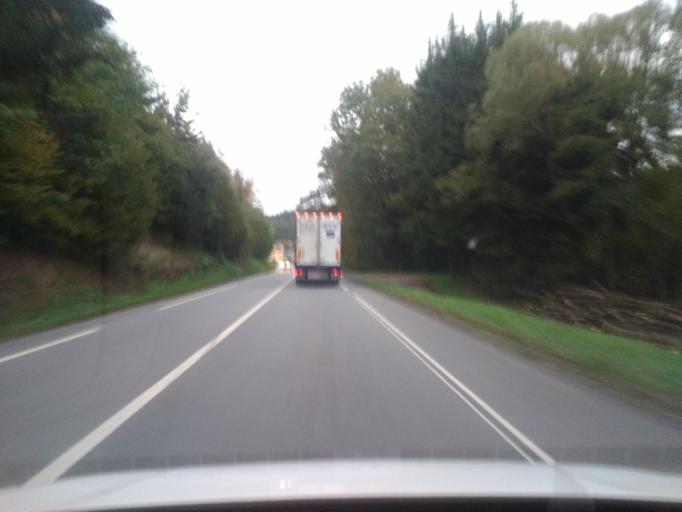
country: FR
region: Lorraine
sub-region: Departement des Vosges
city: Ban-de-Laveline
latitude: 48.2967
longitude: 7.0718
